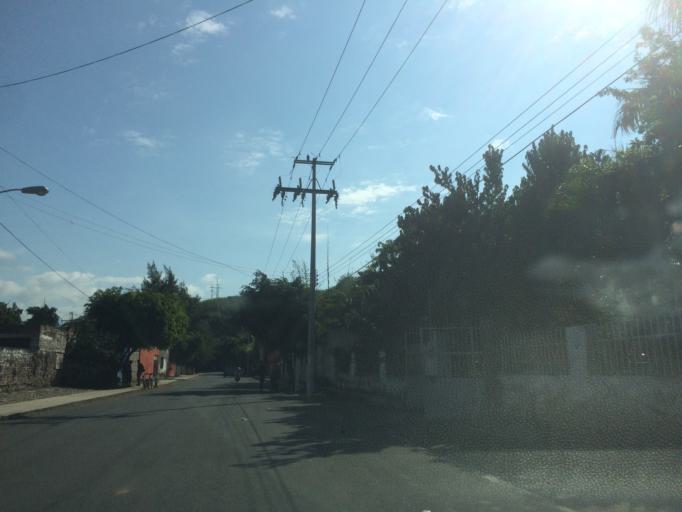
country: MX
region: Nayarit
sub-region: Ahuacatlan
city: Ahuacatlan
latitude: 21.0494
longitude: -104.4779
